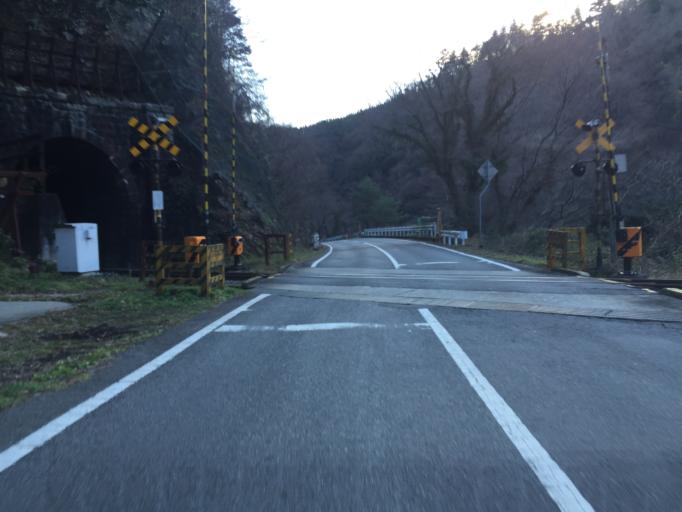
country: JP
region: Fukushima
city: Iwaki
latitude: 37.1561
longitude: 140.8273
